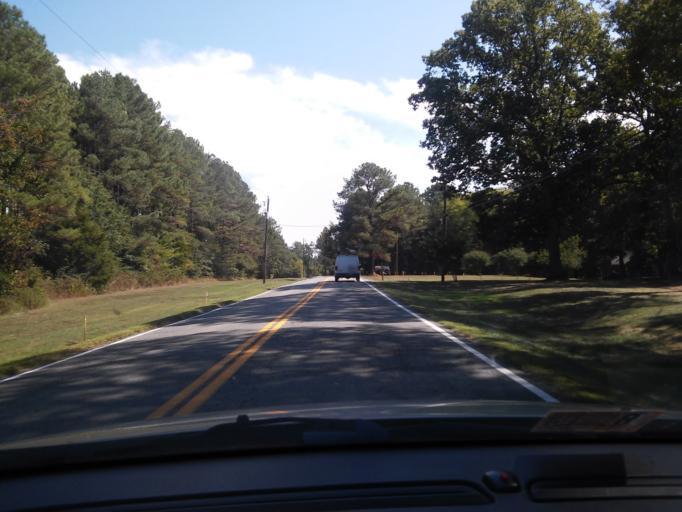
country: US
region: Virginia
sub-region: Henrico County
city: Short Pump
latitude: 37.5583
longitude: -77.6810
